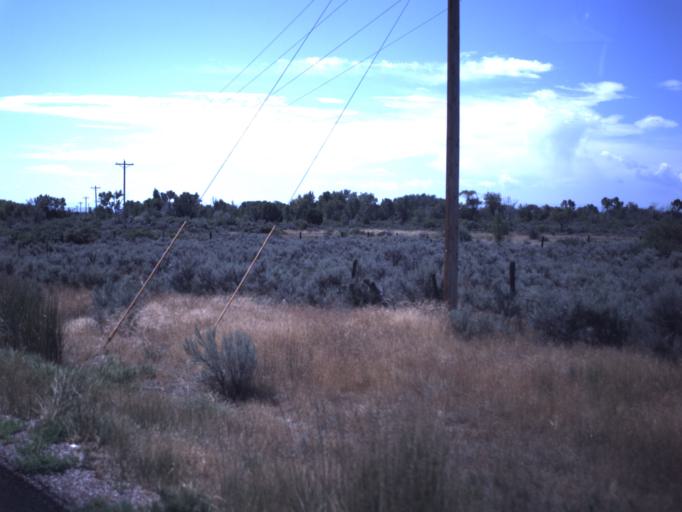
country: US
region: Utah
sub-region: Duchesne County
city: Roosevelt
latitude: 40.4145
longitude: -109.9181
